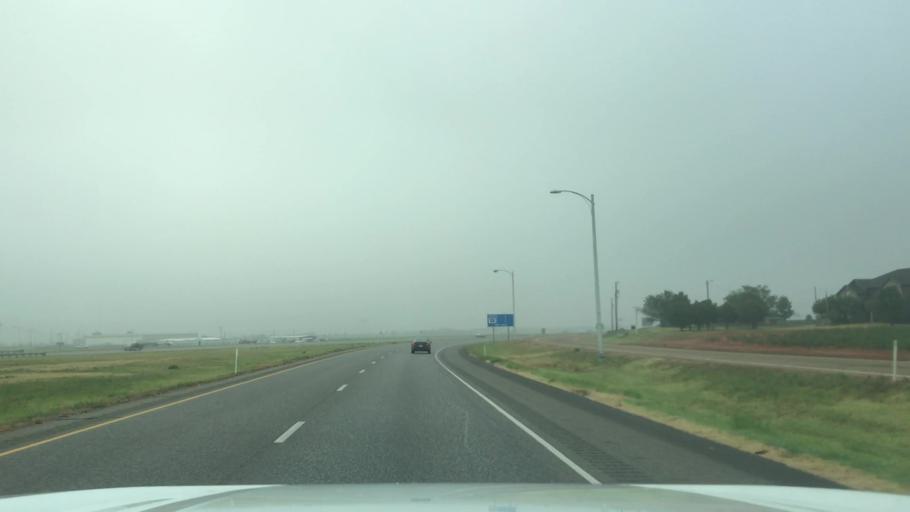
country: US
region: Texas
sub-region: Lubbock County
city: Slaton
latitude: 33.4582
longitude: -101.6689
